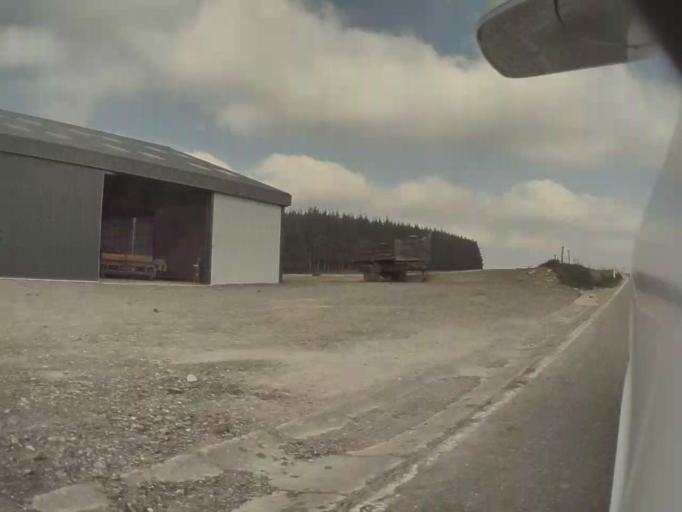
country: BE
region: Wallonia
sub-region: Province du Luxembourg
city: Tellin
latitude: 50.0645
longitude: 5.2044
